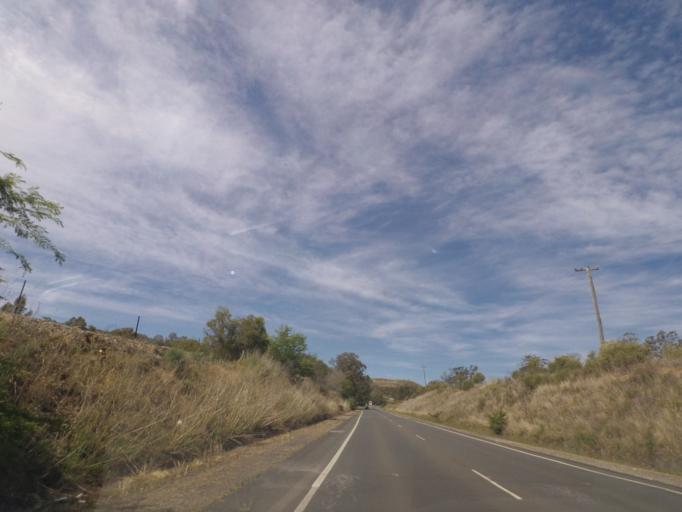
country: AU
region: New South Wales
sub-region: Wollondilly
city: Picton
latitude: -34.1654
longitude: 150.6318
